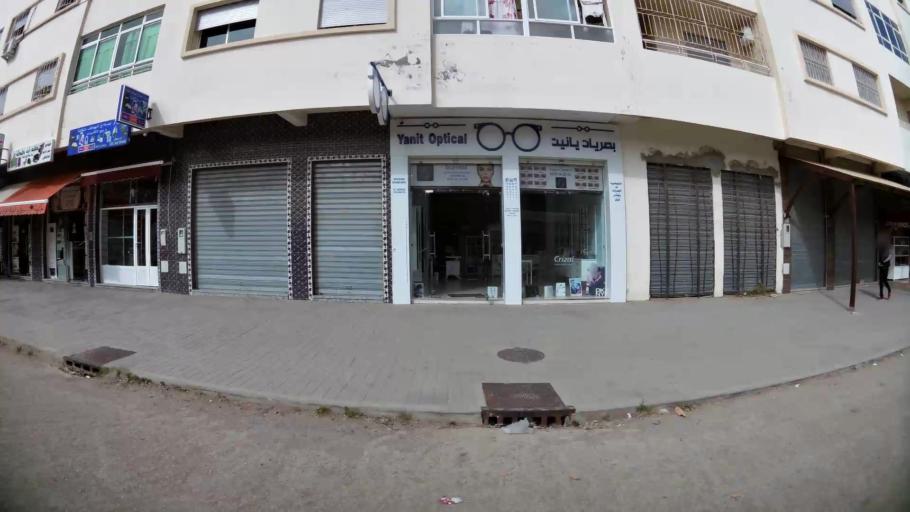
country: MA
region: Tanger-Tetouan
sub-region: Tanger-Assilah
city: Boukhalef
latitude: 35.7063
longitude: -5.9049
